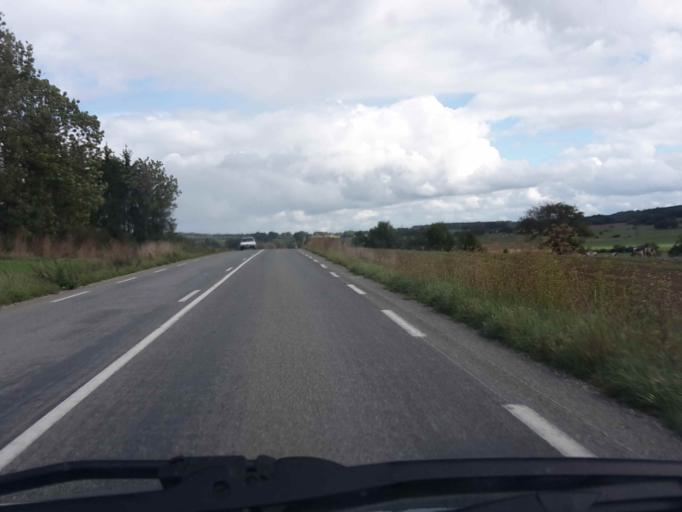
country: FR
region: Franche-Comte
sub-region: Departement du Doubs
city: Saone
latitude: 47.2367
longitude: 6.1033
